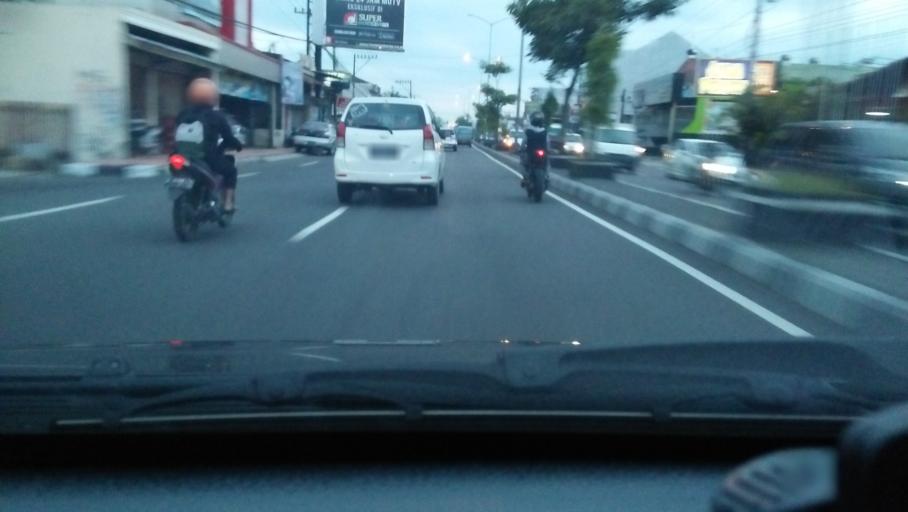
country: ID
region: Central Java
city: Mertoyudan
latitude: -7.5087
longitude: 110.2247
